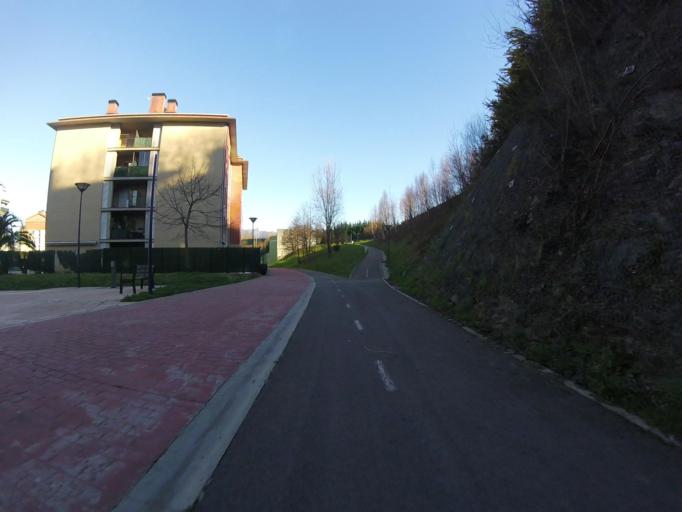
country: ES
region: Basque Country
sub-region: Provincia de Guipuzcoa
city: Errenteria
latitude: 43.3074
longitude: -1.8908
